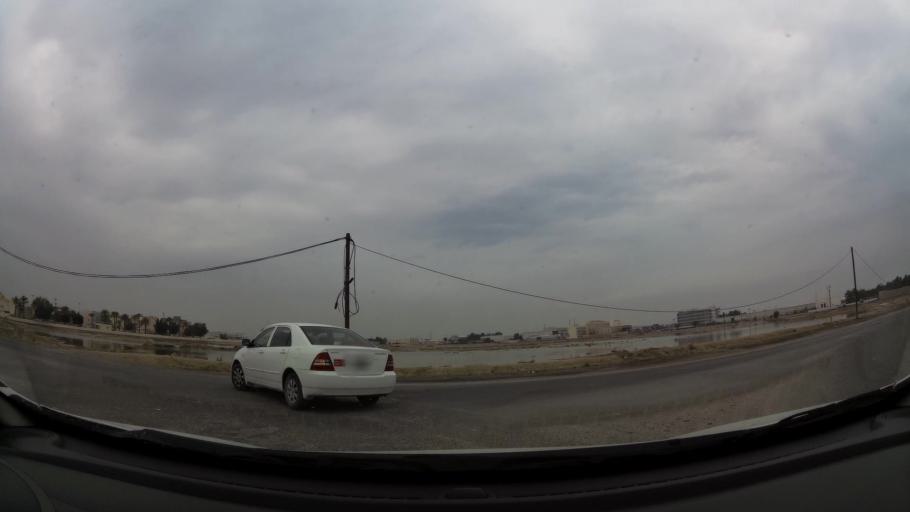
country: BH
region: Northern
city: Sitrah
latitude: 26.1703
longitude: 50.6193
